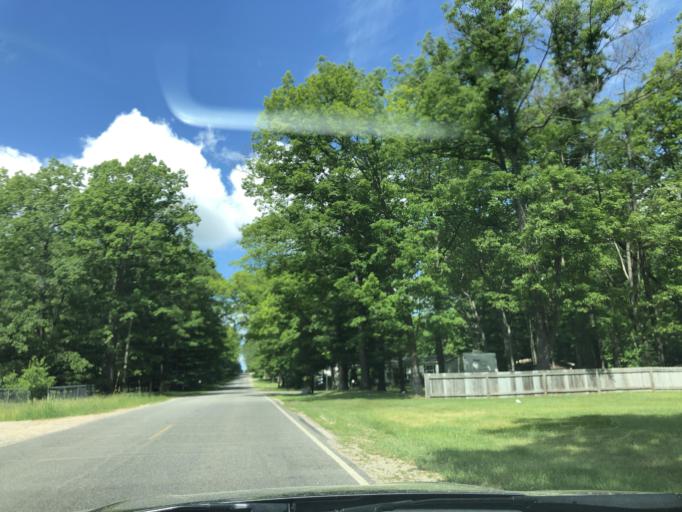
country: US
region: Michigan
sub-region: Clare County
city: Harrison
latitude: 44.0315
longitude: -84.8114
